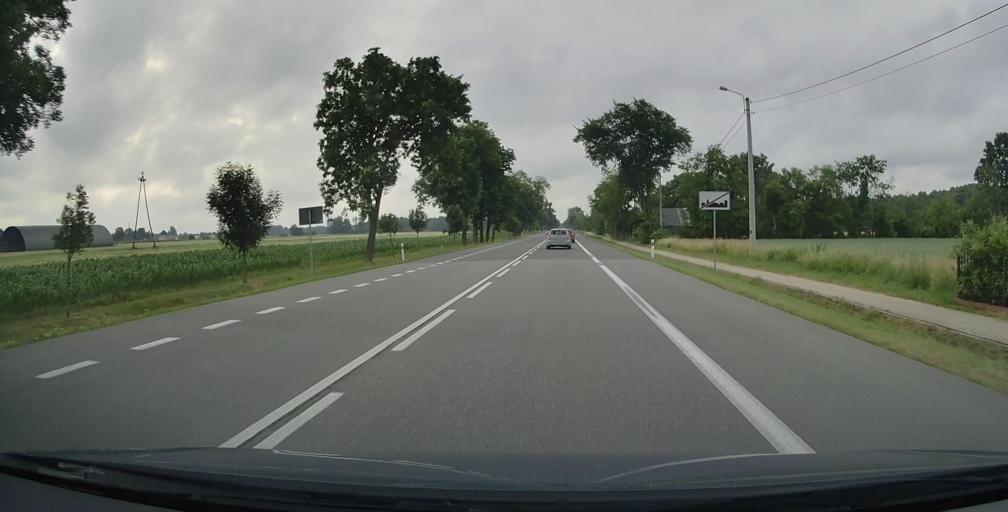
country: PL
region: Lublin Voivodeship
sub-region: Powiat lukowski
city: Trzebieszow
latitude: 52.0683
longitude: 22.5304
